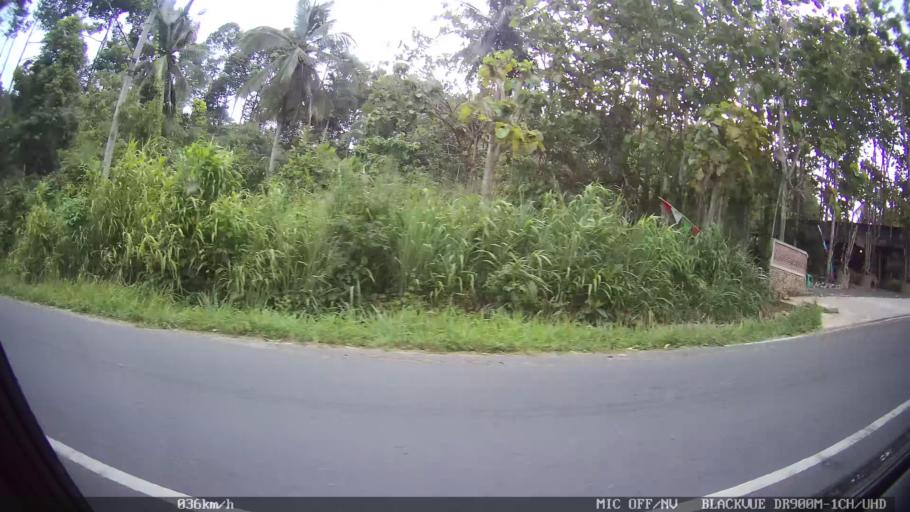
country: ID
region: Lampung
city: Bandarlampung
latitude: -5.4111
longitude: 105.2253
